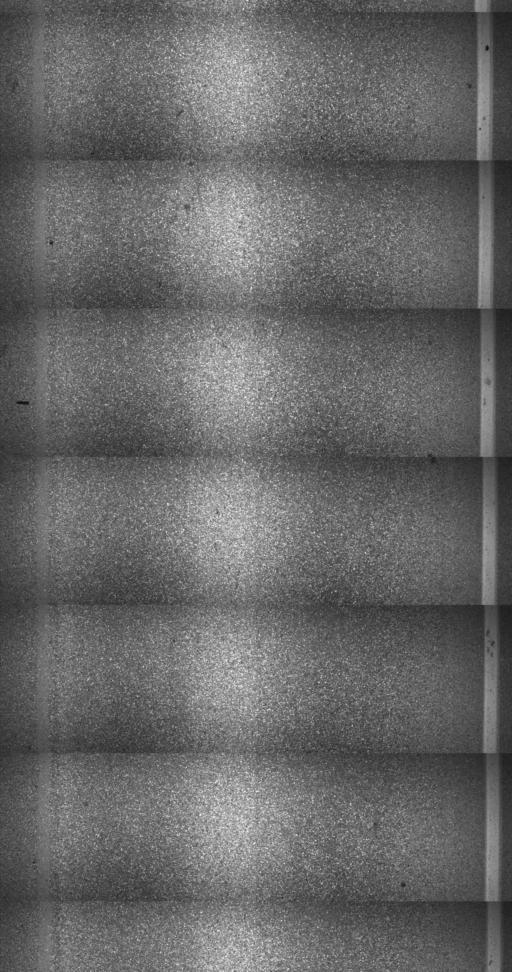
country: US
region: Vermont
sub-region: Lamoille County
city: Johnson
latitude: 44.6616
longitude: -72.7724
